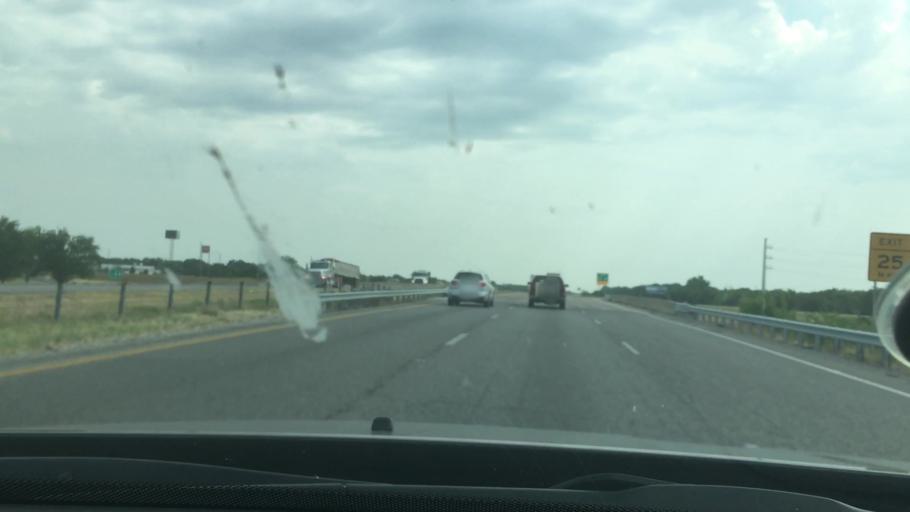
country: US
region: Oklahoma
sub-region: Bryan County
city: Durant
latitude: 34.0192
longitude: -96.3901
